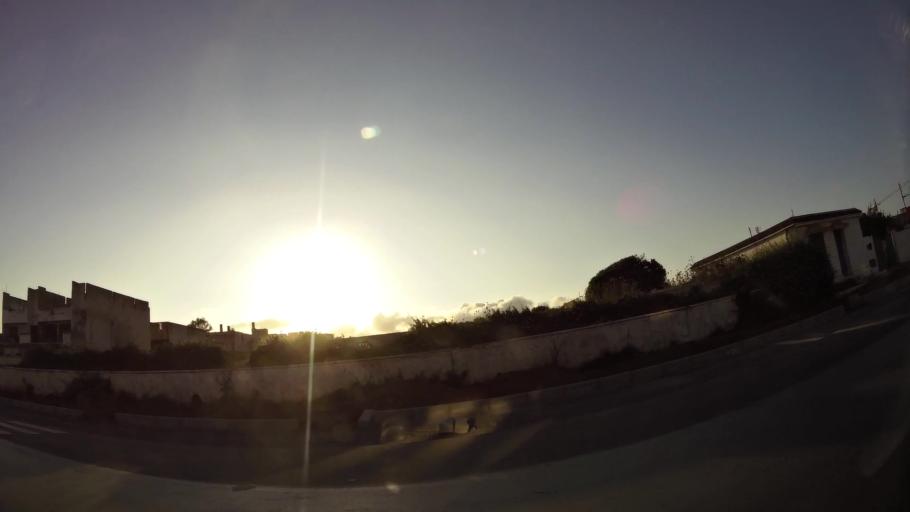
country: MA
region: Rabat-Sale-Zemmour-Zaer
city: Sale
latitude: 34.1224
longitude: -6.7397
